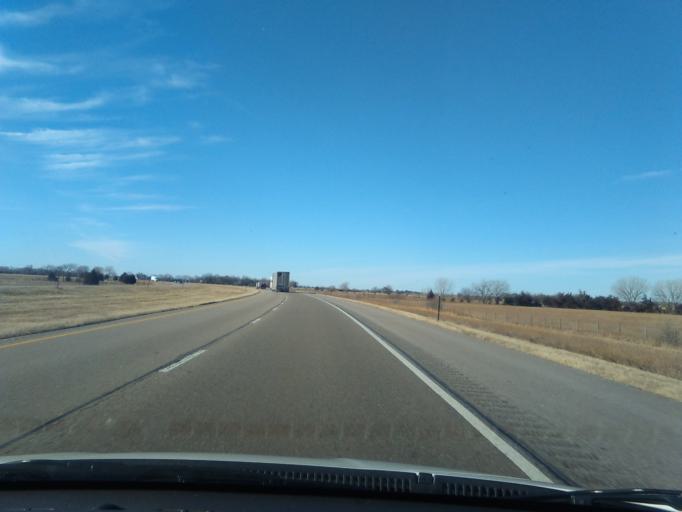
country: US
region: Nebraska
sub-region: Hall County
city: Grand Island
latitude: 40.8237
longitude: -98.4038
